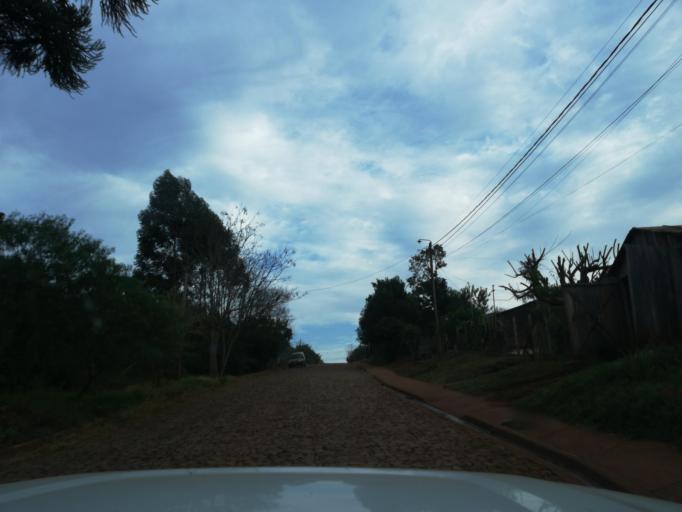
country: AR
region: Misiones
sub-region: Departamento de San Pedro
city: San Pedro
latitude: -26.6270
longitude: -54.0949
